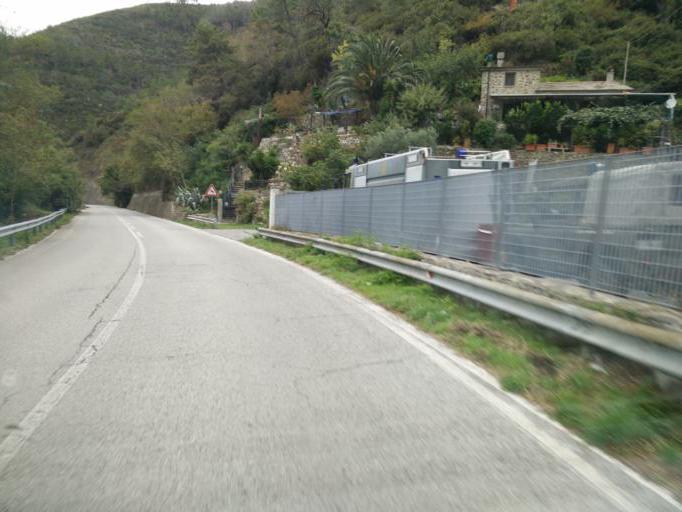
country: IT
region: Liguria
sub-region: Provincia di La Spezia
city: Riomaggiore
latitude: 44.1019
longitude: 9.7510
